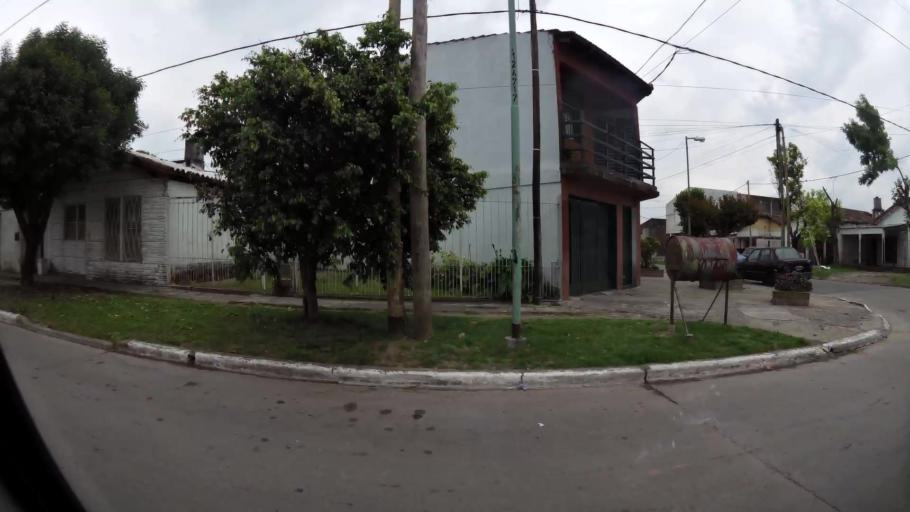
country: AR
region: Buenos Aires
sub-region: Partido de La Plata
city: La Plata
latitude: -34.9096
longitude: -57.9914
